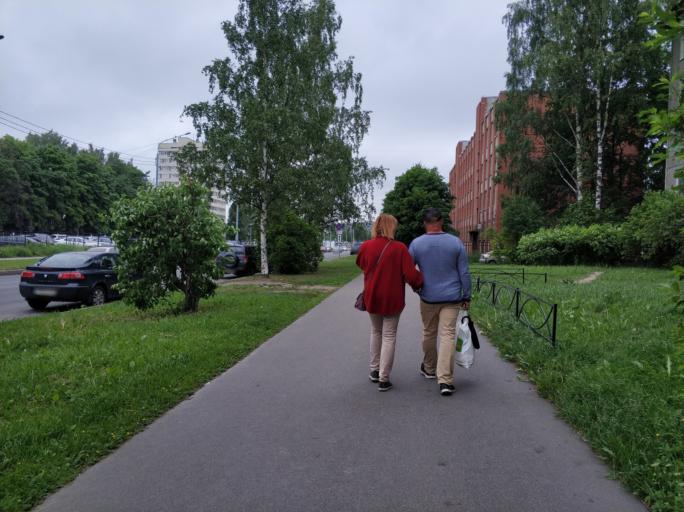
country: RU
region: St.-Petersburg
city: Grazhdanka
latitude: 60.0429
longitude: 30.4163
